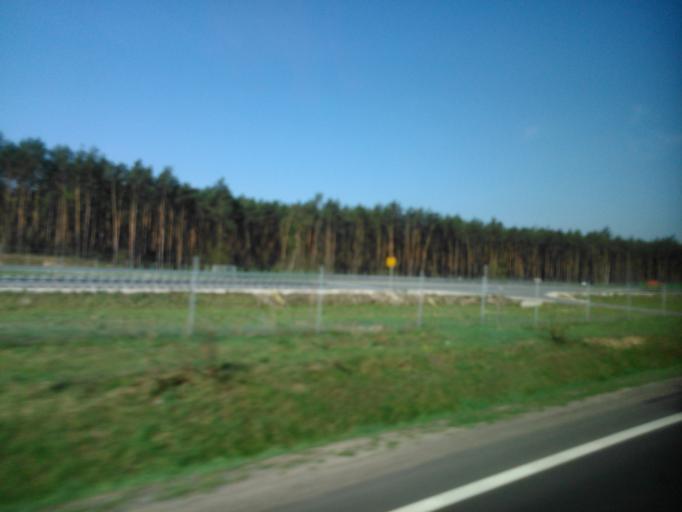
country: PL
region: Kujawsko-Pomorskie
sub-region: Powiat aleksandrowski
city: Aleksandrow Kujawski
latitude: 52.8855
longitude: 18.7372
